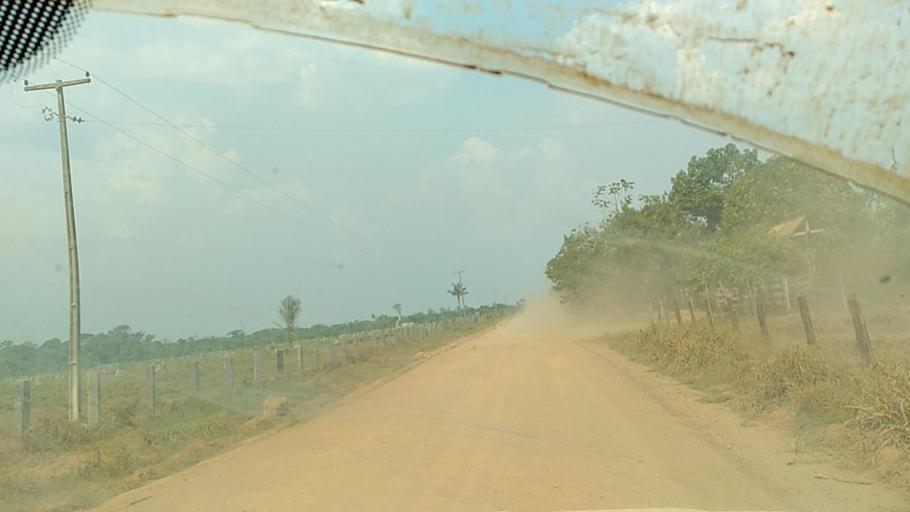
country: BR
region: Rondonia
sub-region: Porto Velho
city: Porto Velho
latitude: -8.6832
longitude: -63.2160
